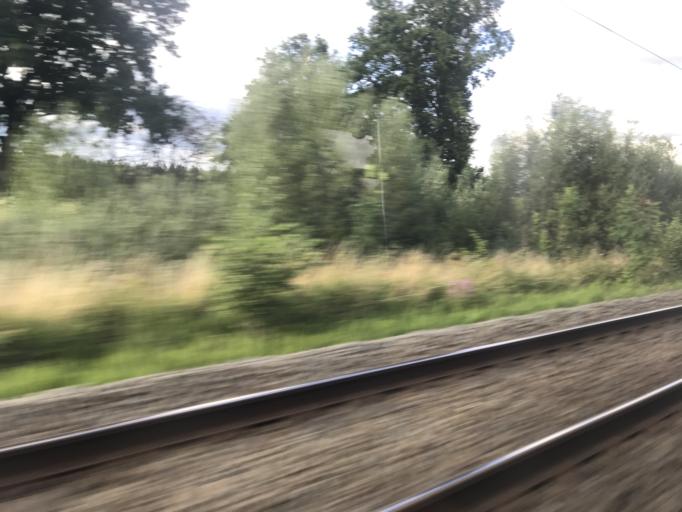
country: FR
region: Champagne-Ardenne
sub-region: Departement des Ardennes
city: Douzy
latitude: 49.6725
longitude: 5.0148
